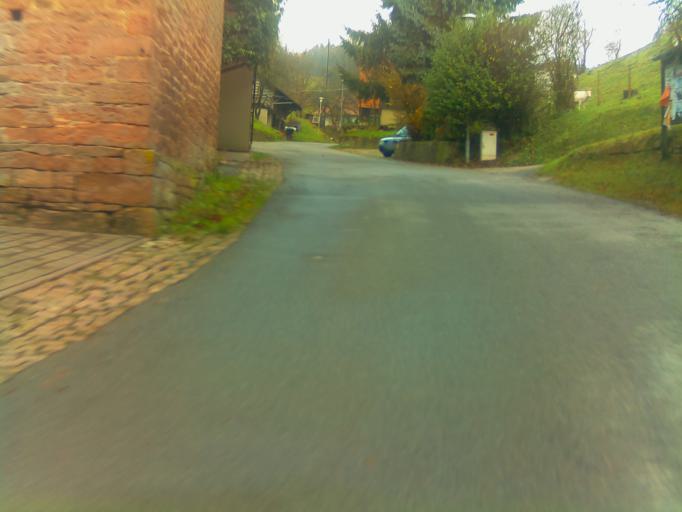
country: DE
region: Baden-Wuerttemberg
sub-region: Karlsruhe Region
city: Heddesbach
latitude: 49.4887
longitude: 8.8676
